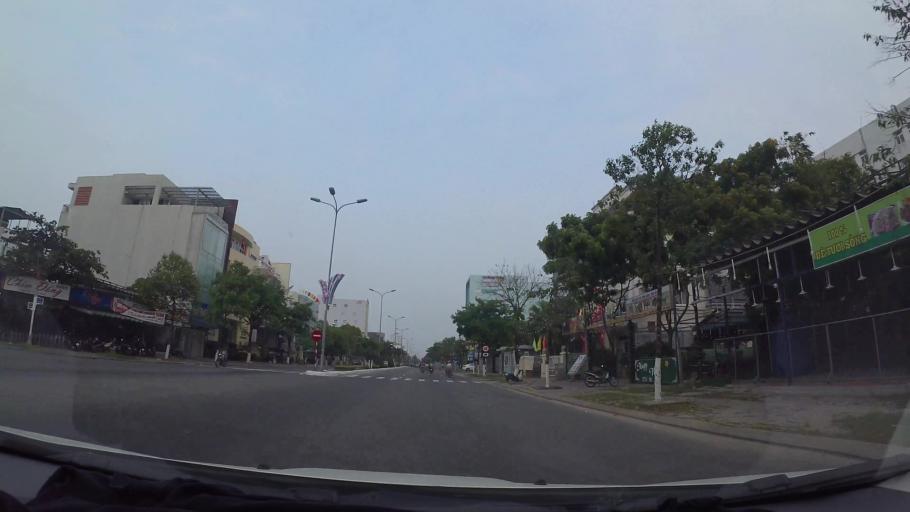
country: VN
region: Da Nang
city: Cam Le
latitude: 16.0320
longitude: 108.2160
